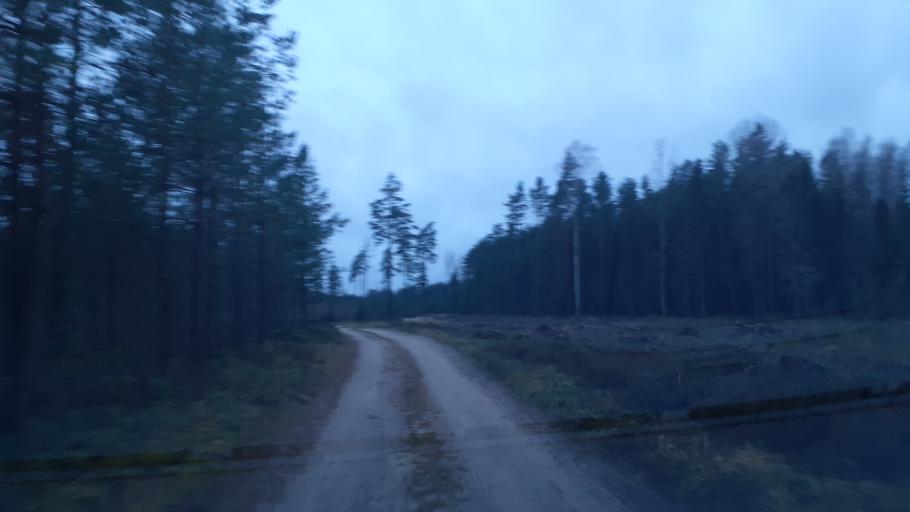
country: LV
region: Kuldigas Rajons
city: Kuldiga
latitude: 56.9958
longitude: 22.0548
